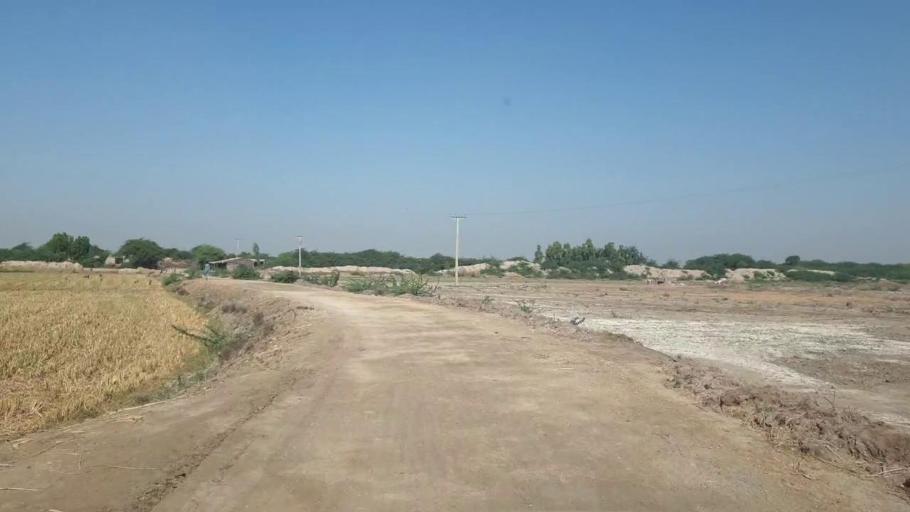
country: PK
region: Sindh
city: Talhar
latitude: 24.8015
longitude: 68.7903
